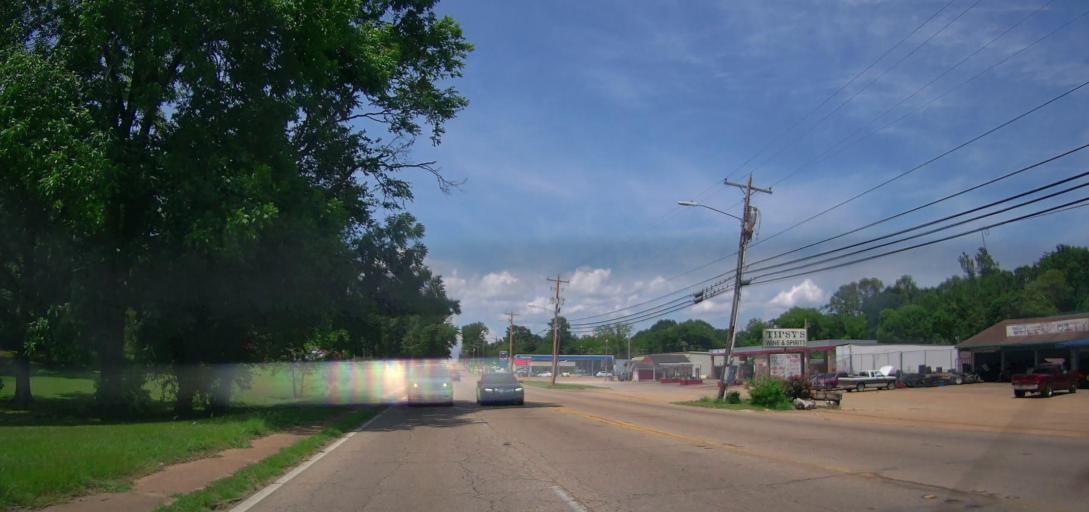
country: US
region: Mississippi
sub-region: Lee County
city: Verona
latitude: 34.1970
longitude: -88.7201
